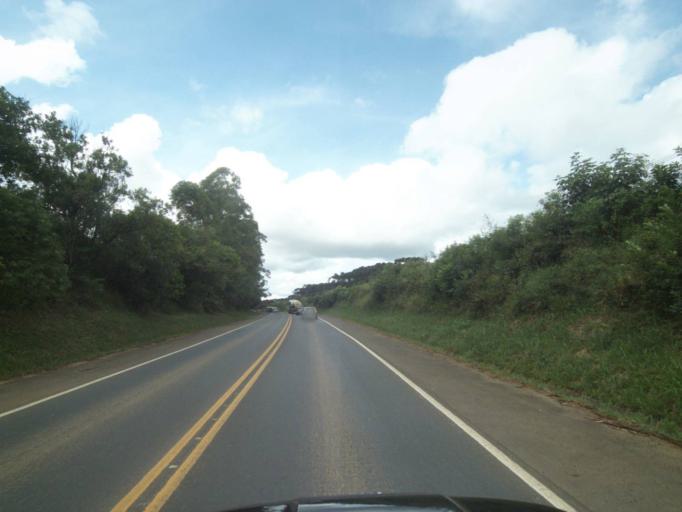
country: BR
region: Parana
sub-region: Telemaco Borba
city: Telemaco Borba
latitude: -24.3689
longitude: -50.6599
